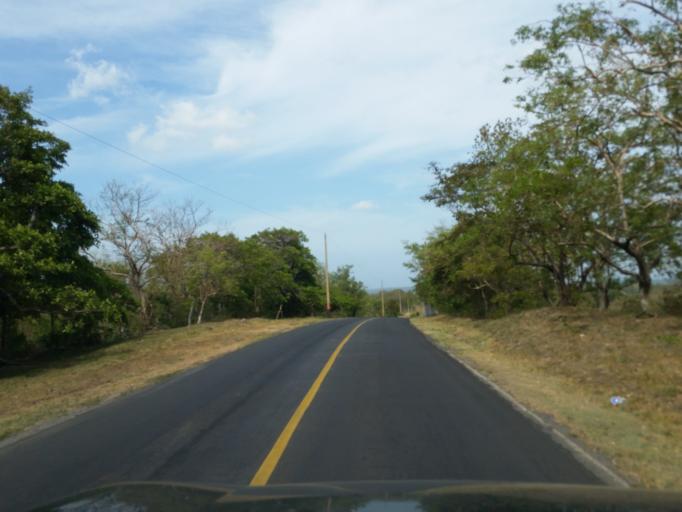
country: NI
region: Managua
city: San Rafael del Sur
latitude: 11.9017
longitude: -86.3873
